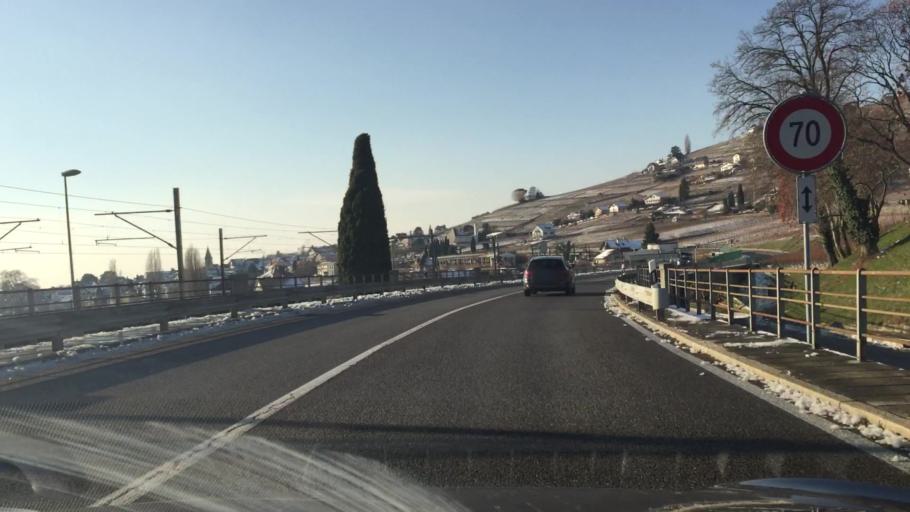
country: CH
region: Vaud
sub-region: Lavaux-Oron District
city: Cully
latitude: 46.4900
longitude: 6.7399
